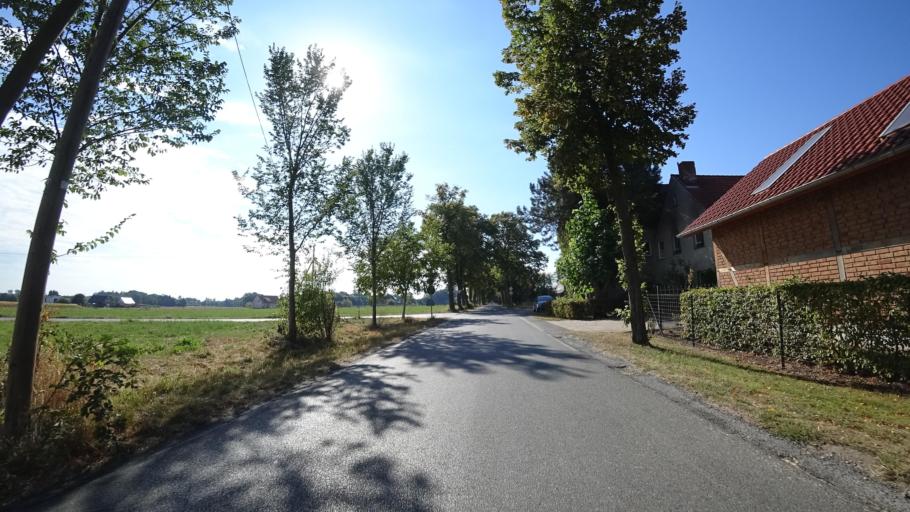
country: DE
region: North Rhine-Westphalia
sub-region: Regierungsbezirk Detmold
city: Rheda-Wiedenbruck
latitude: 51.8703
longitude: 8.2742
